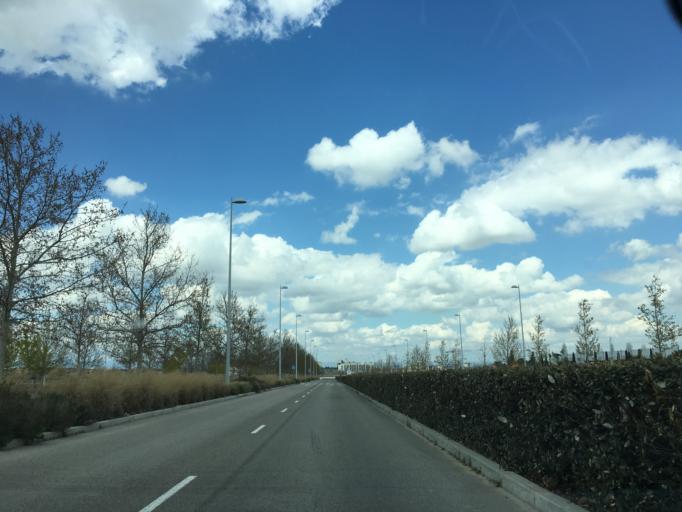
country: ES
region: Madrid
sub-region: Provincia de Madrid
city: Hortaleza
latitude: 40.4776
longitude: -3.6179
